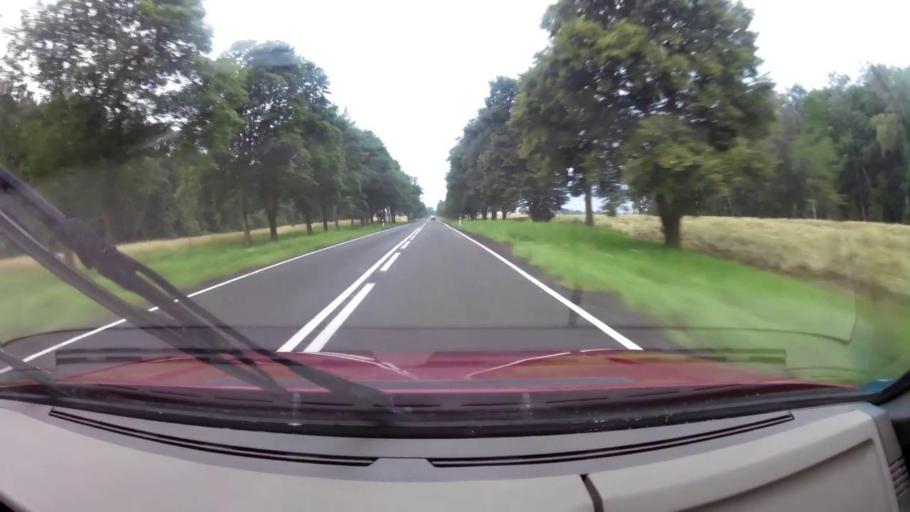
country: PL
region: West Pomeranian Voivodeship
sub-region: Powiat stargardzki
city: Stara Dabrowa
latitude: 53.3713
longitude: 15.1325
